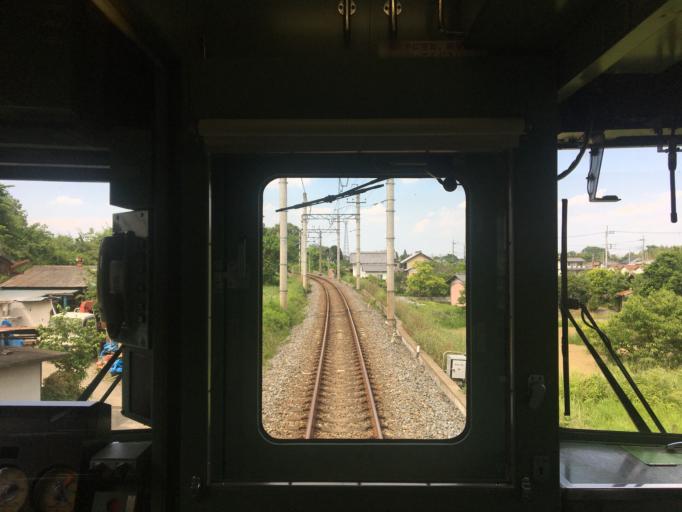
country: JP
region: Saitama
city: Yorii
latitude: 36.1002
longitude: 139.2354
